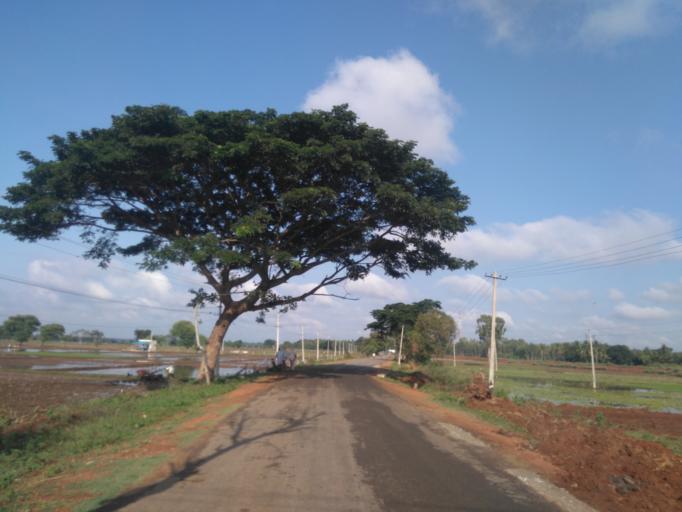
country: IN
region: Karnataka
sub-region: Mysore
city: Tirumakudal Narsipur
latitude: 12.2586
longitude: 77.0056
